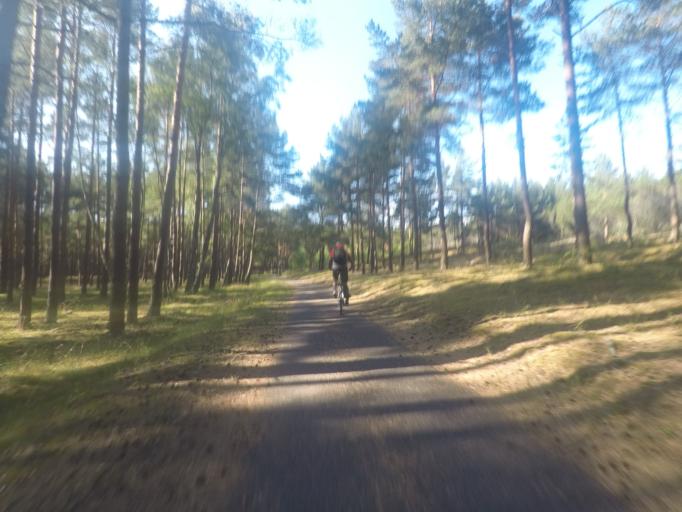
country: LT
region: Klaipedos apskritis
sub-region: Klaipeda
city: Klaipeda
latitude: 55.5799
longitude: 21.1137
